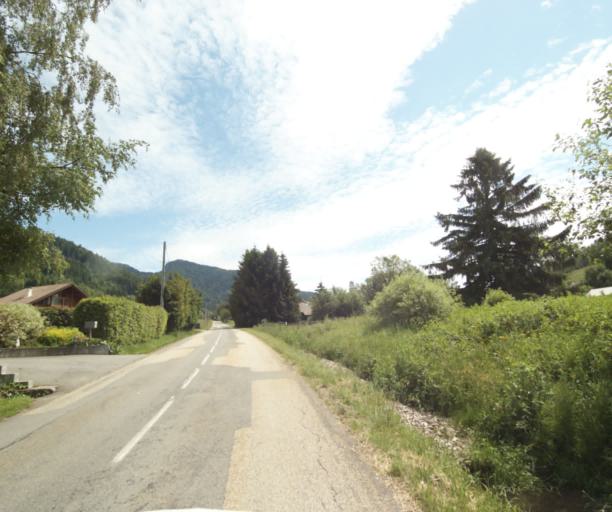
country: FR
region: Rhone-Alpes
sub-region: Departement de la Haute-Savoie
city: Perrignier
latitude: 46.2976
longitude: 6.4736
